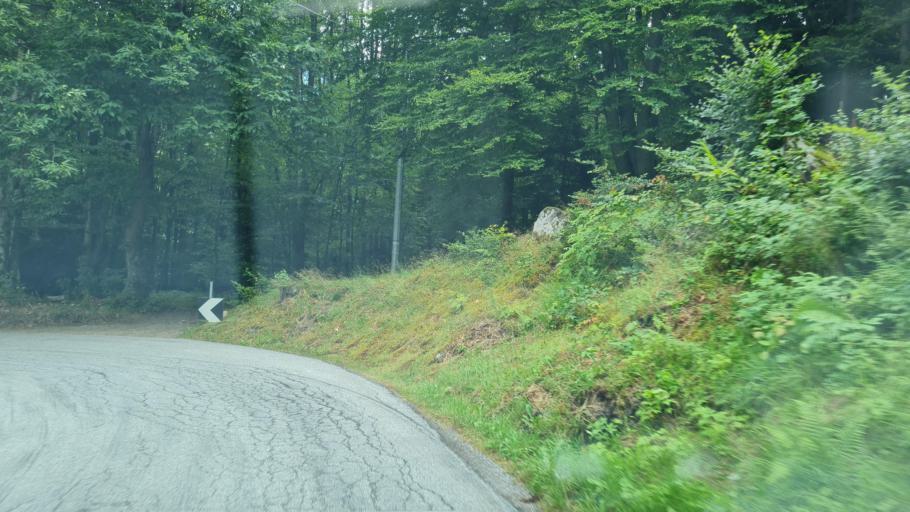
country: IT
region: Piedmont
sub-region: Provincia Verbano-Cusio-Ossola
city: Baceno
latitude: 46.2463
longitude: 8.3165
